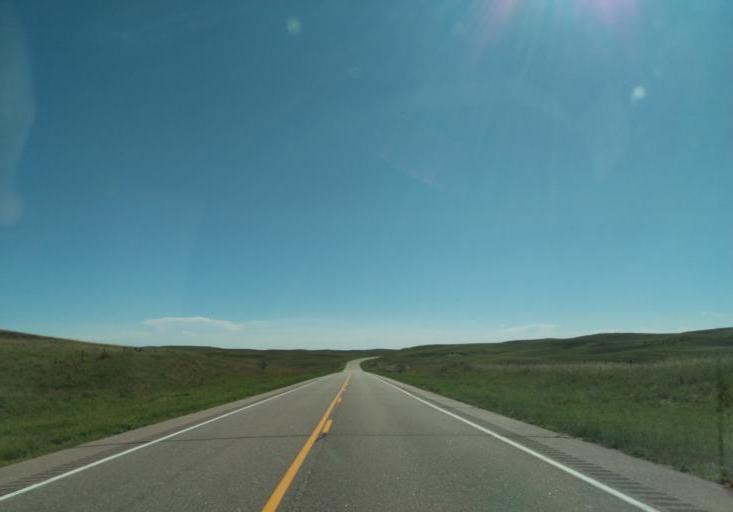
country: US
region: South Dakota
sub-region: Bennett County
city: Martin
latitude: 42.9371
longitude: -101.2905
